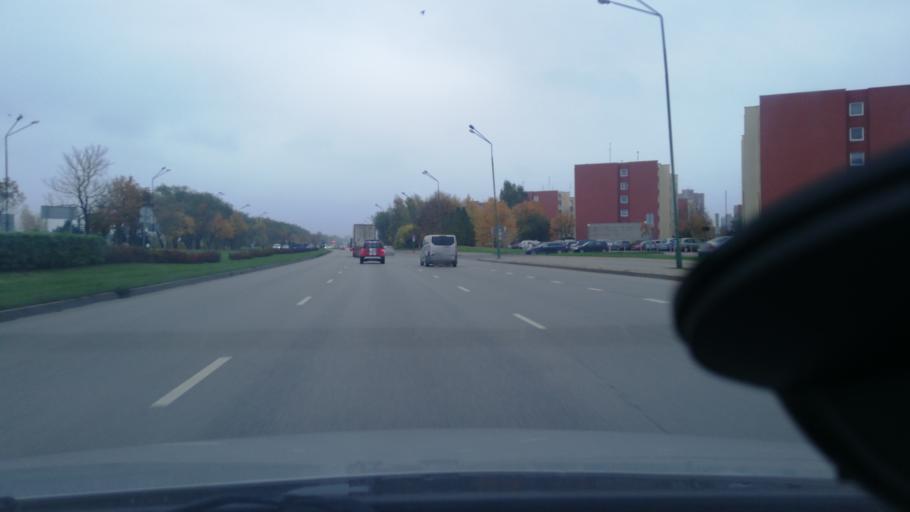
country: LT
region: Klaipedos apskritis
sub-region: Klaipeda
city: Klaipeda
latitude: 55.6771
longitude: 21.1896
